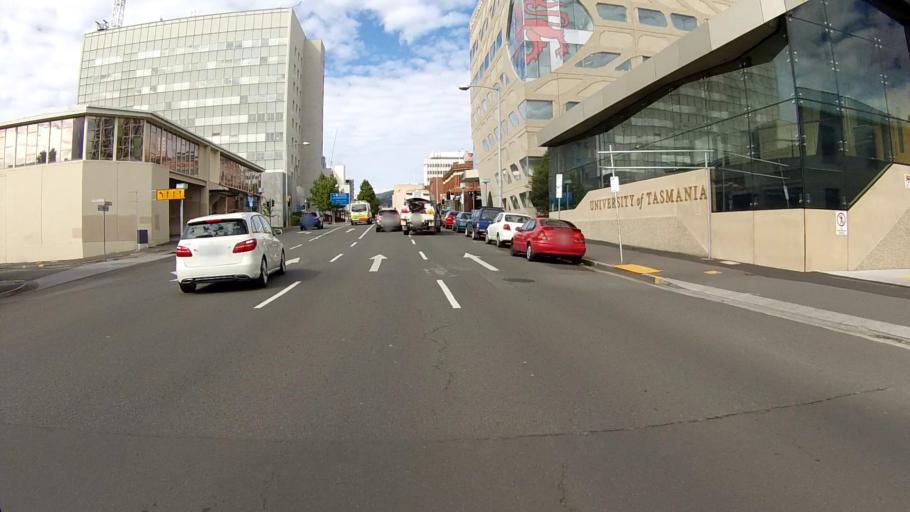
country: AU
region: Tasmania
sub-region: Hobart
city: Hobart
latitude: -42.8785
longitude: 147.3305
